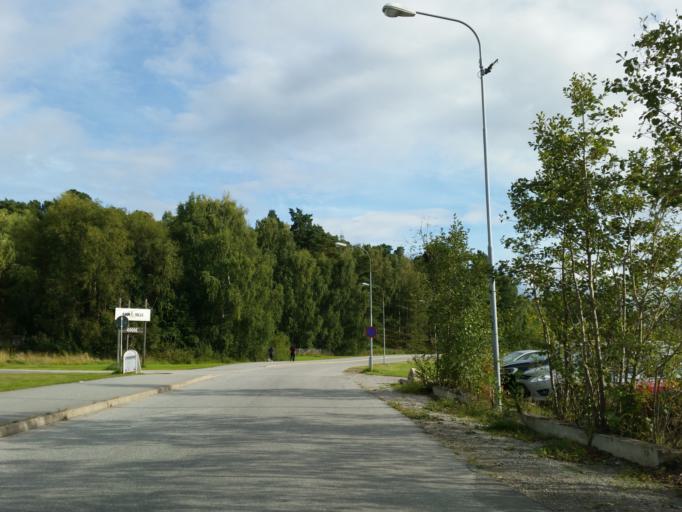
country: SE
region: Stockholm
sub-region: Sollentuna Kommun
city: Sollentuna
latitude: 59.4520
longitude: 17.9298
